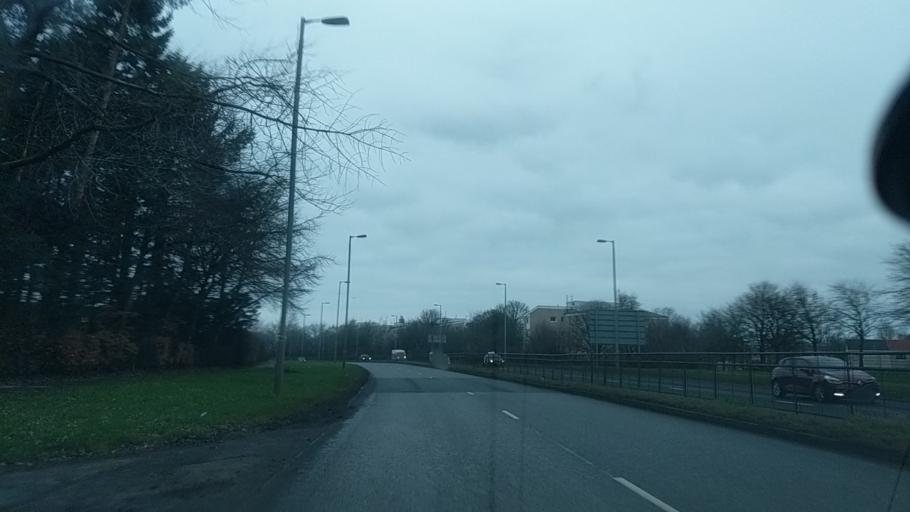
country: GB
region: Scotland
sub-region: South Lanarkshire
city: East Kilbride
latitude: 55.7590
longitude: -4.1653
